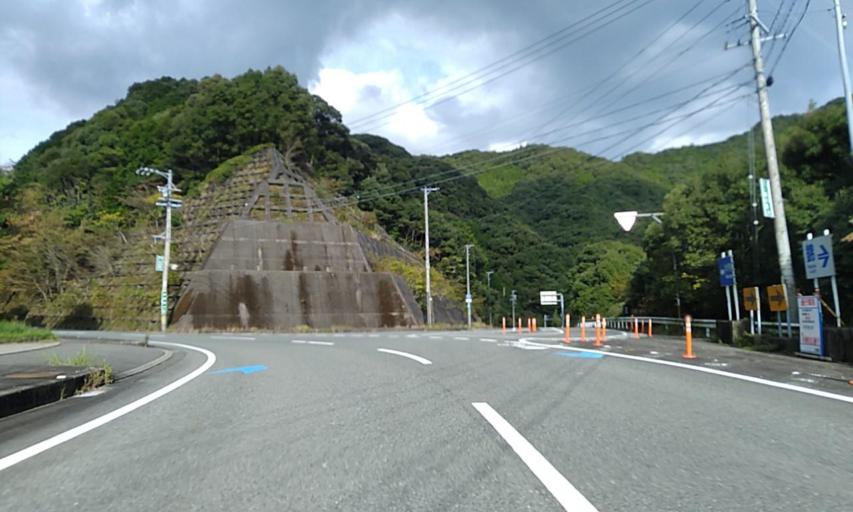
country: JP
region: Mie
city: Owase
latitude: 34.2499
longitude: 136.4039
